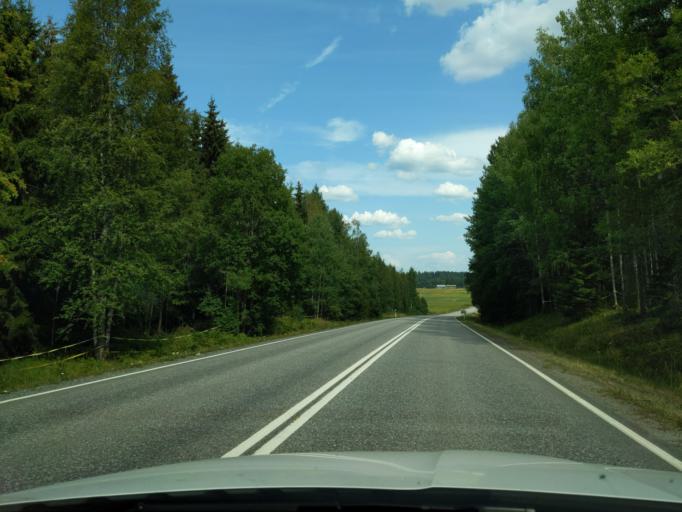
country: FI
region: Haeme
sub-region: Haemeenlinna
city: Lammi
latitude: 61.1212
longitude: 24.9423
